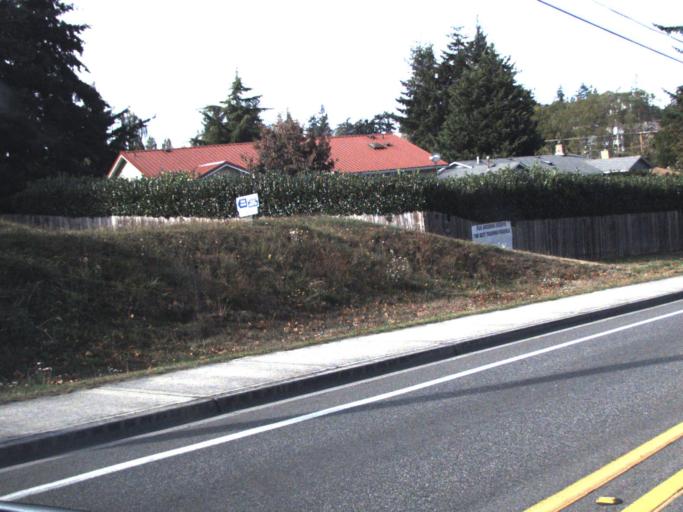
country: US
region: Washington
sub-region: Island County
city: Oak Harbor
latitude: 48.2824
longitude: -122.6694
